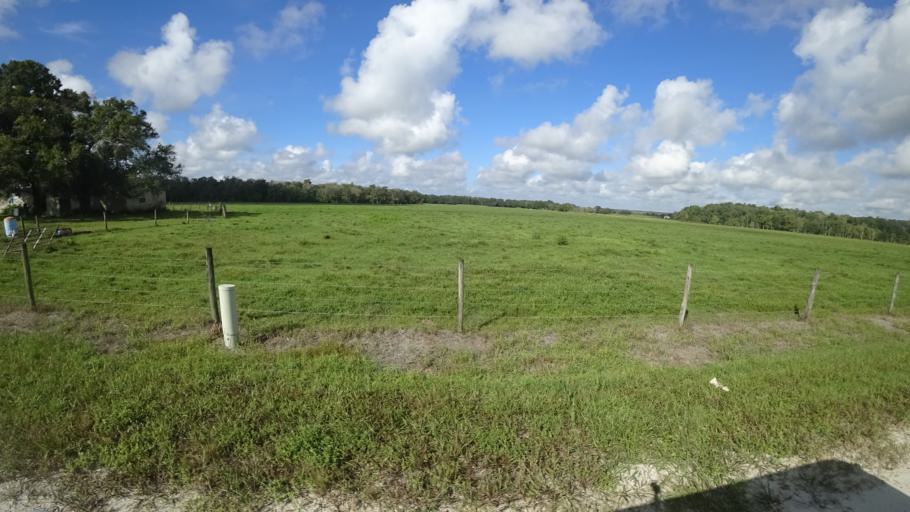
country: US
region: Florida
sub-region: Sarasota County
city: Lake Sarasota
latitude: 27.3304
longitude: -82.2041
